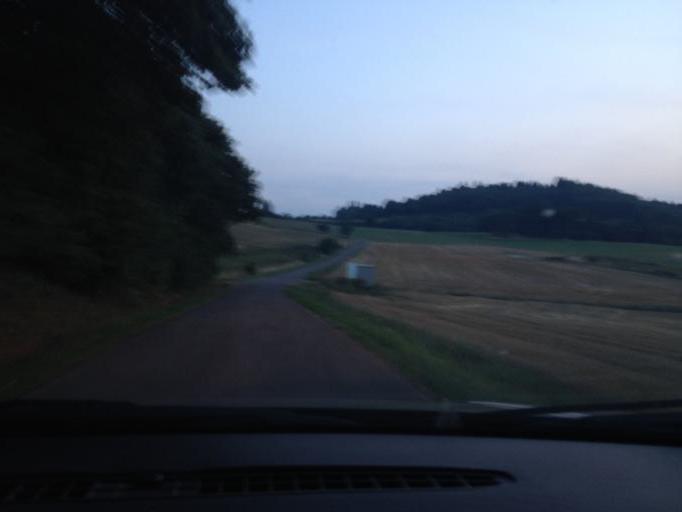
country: DE
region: Saarland
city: Namborn
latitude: 49.5457
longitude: 7.1303
